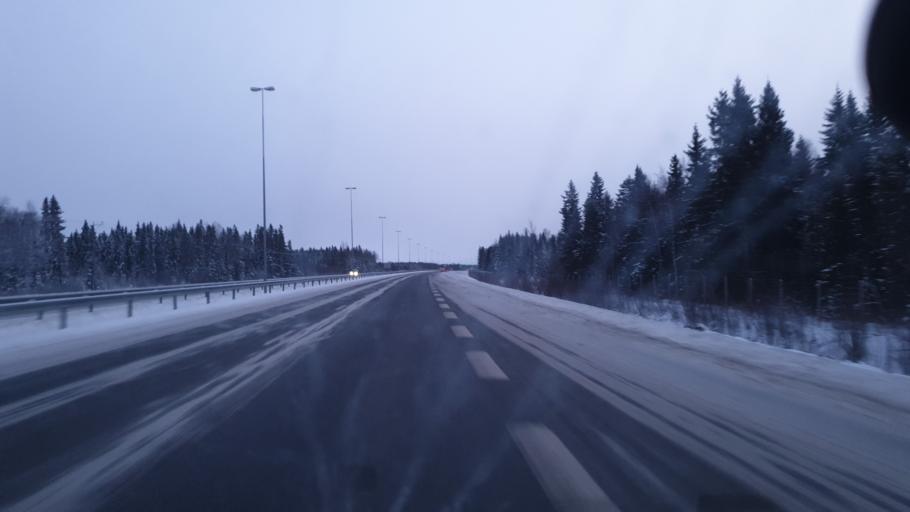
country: FI
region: Lapland
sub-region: Kemi-Tornio
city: Tornio
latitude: 65.8383
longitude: 24.2939
